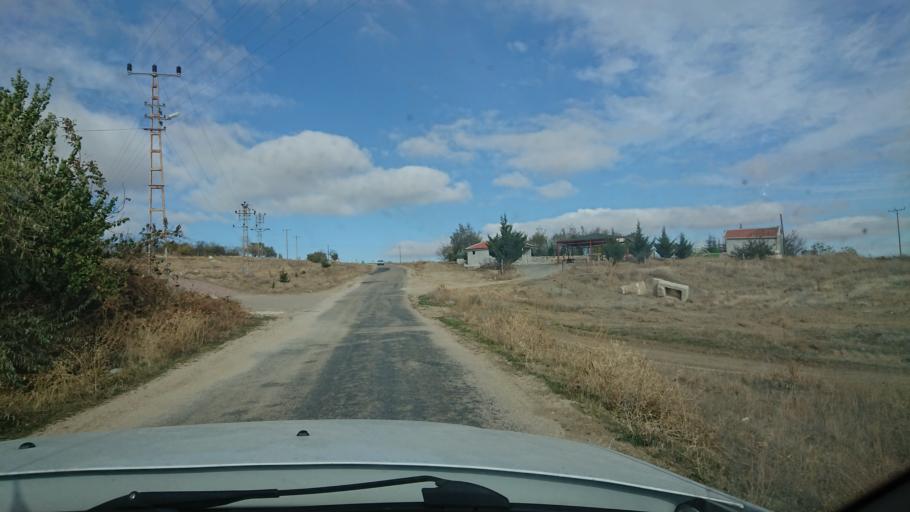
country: TR
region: Aksaray
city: Agacoren
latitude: 38.8121
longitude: 33.9836
